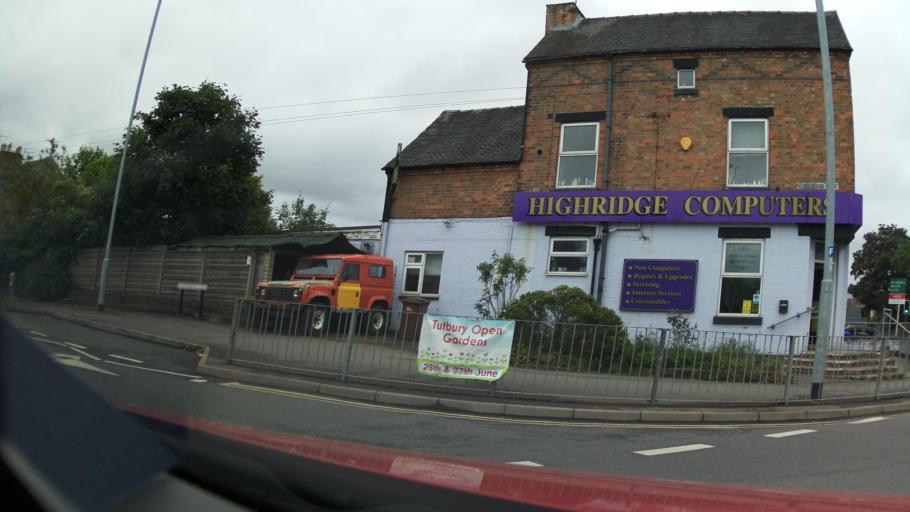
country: GB
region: England
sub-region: Staffordshire
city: Burton upon Trent
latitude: 52.8306
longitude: -1.6528
